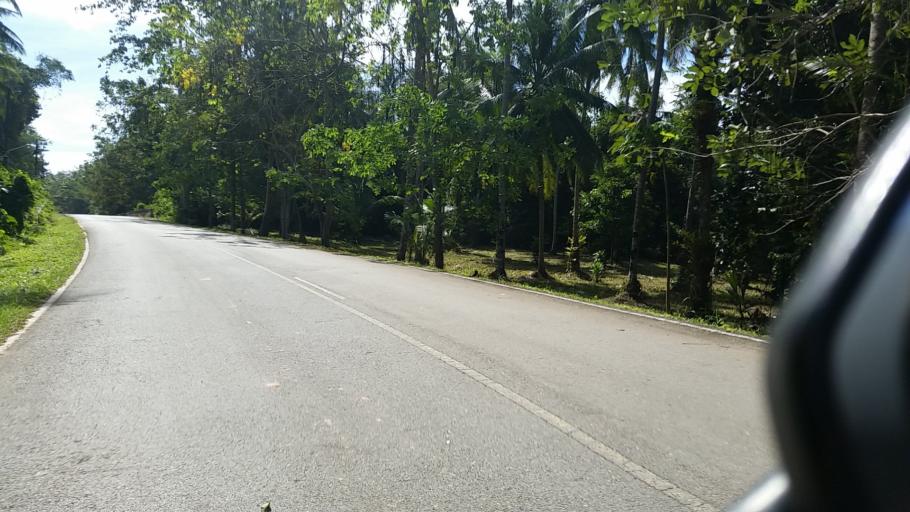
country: TH
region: Trat
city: Ko Chang Tai
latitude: 11.9903
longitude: 102.3969
